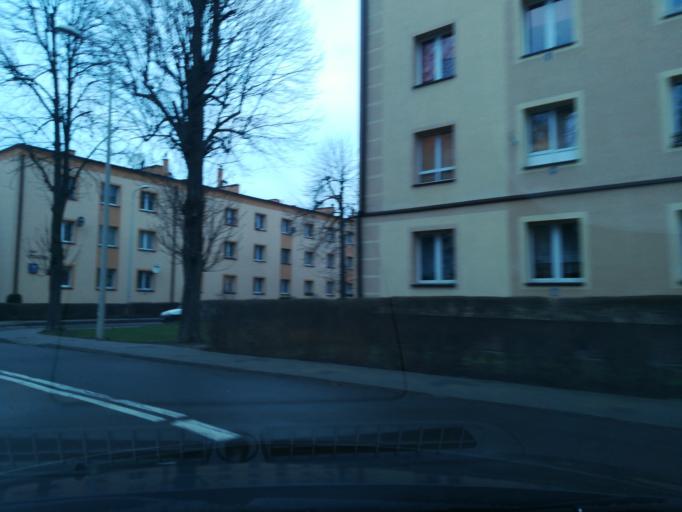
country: PL
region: Subcarpathian Voivodeship
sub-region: Rzeszow
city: Rzeszow
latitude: 50.0265
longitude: 21.9940
